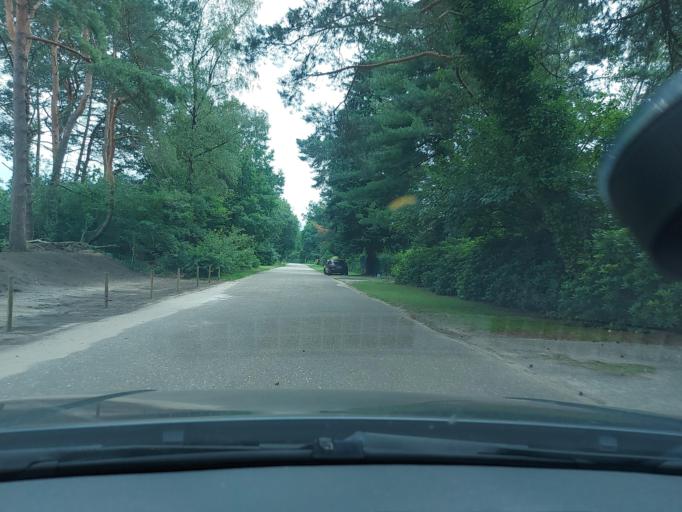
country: BE
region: Flanders
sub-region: Provincie Antwerpen
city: Balen
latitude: 51.1965
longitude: 5.2017
